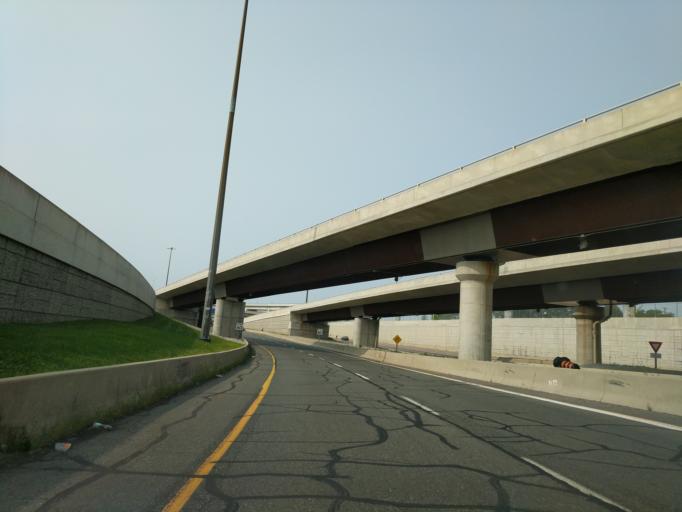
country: CA
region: Ontario
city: Etobicoke
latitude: 43.6966
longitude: -79.6097
